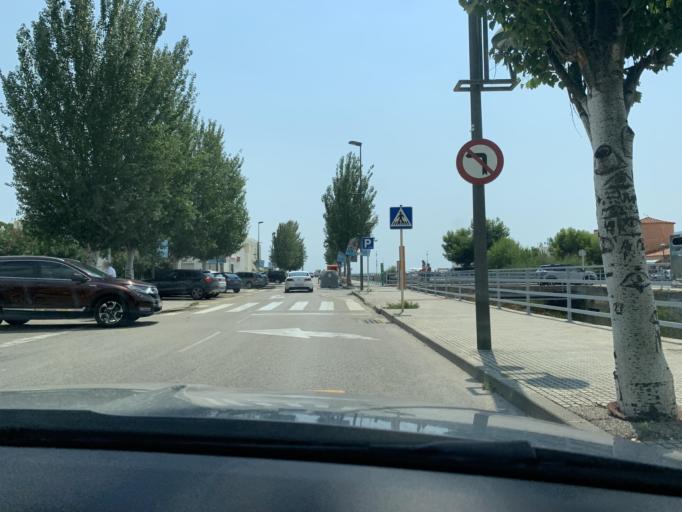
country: ES
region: Catalonia
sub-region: Provincia de Tarragona
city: Altafulla
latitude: 41.1301
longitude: 1.3454
